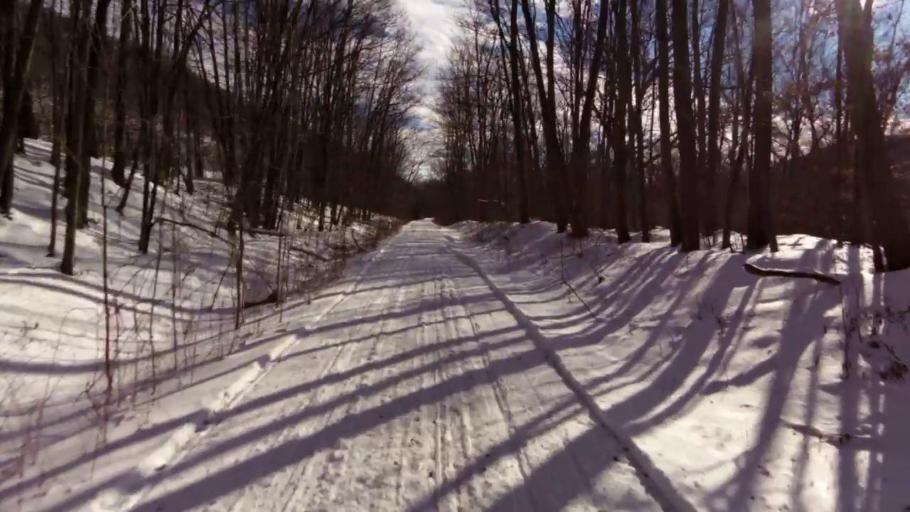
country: US
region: Pennsylvania
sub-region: McKean County
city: Foster Brook
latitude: 42.0622
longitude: -78.6382
